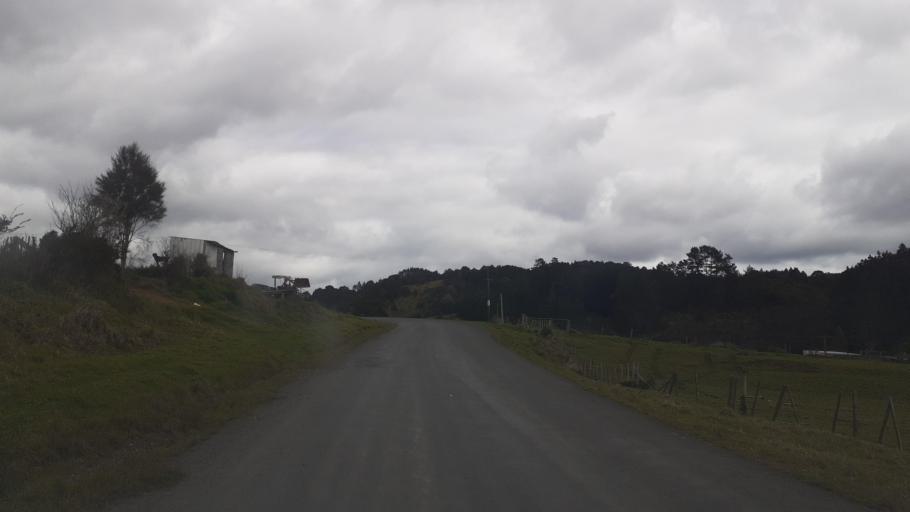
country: NZ
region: Northland
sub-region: Far North District
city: Moerewa
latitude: -35.5863
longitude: 173.9733
